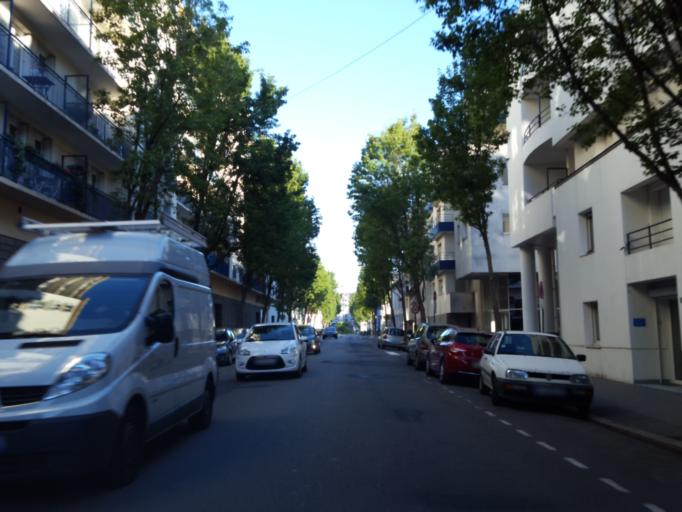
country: FR
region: Pays de la Loire
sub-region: Departement de la Loire-Atlantique
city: Nantes
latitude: 47.2111
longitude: -1.5710
